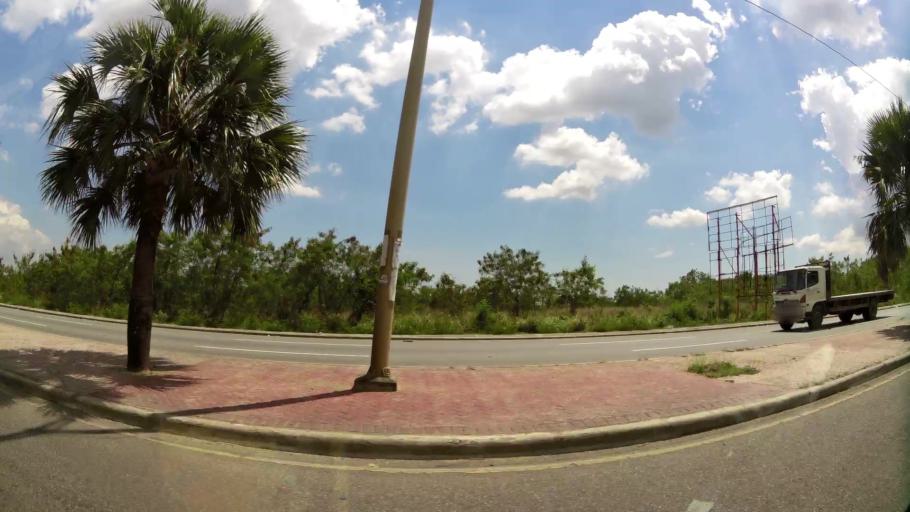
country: DO
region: Nacional
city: La Agustina
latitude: 18.5562
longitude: -69.9414
